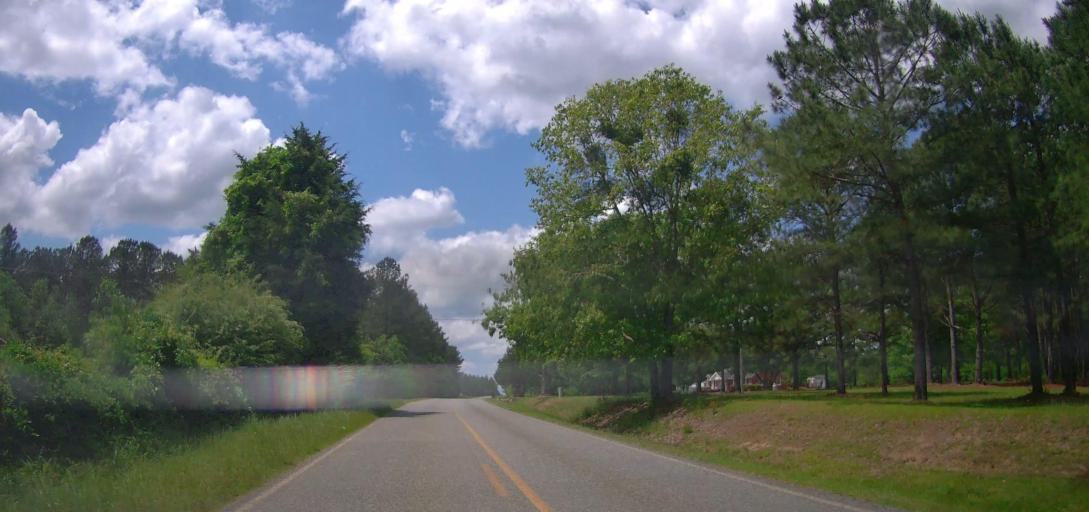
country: US
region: Georgia
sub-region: Laurens County
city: Dublin
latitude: 32.5948
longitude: -83.0202
